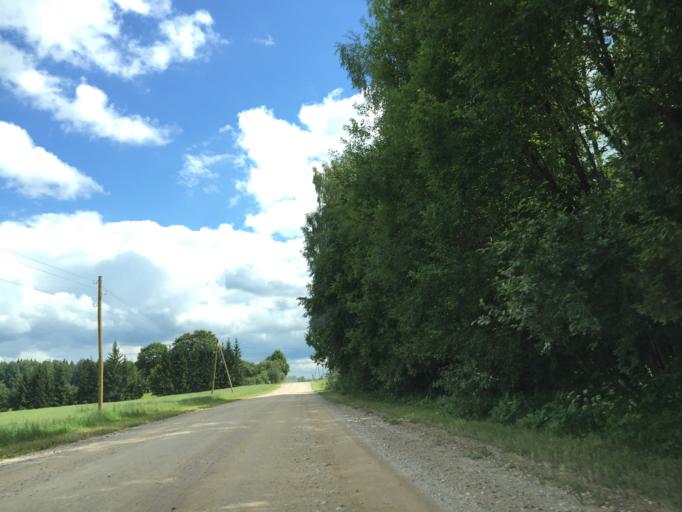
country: LV
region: Malpils
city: Malpils
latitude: 56.8735
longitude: 25.0038
